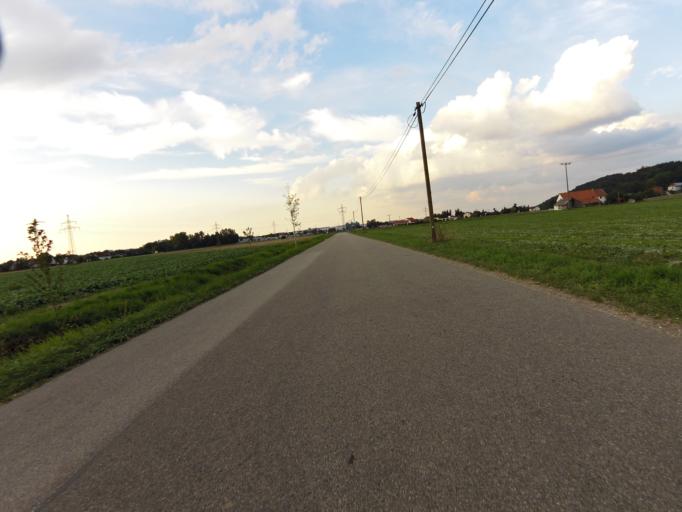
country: DE
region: Bavaria
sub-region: Lower Bavaria
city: Eching
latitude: 48.4813
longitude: 12.0203
